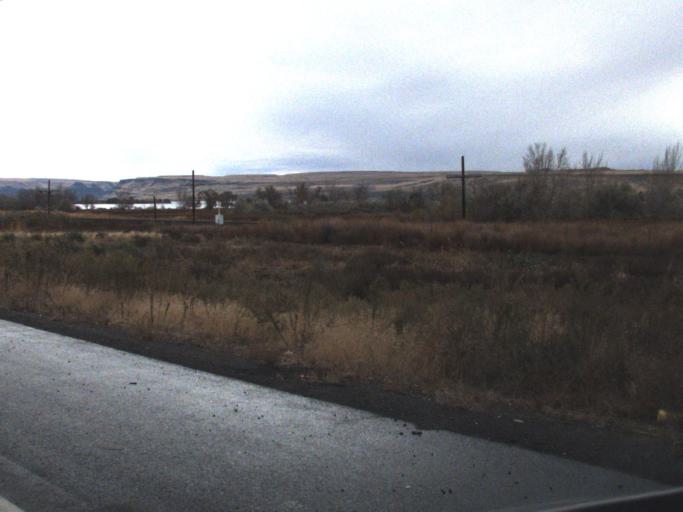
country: US
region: Washington
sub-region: Benton County
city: Finley
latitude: 46.1331
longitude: -118.9340
